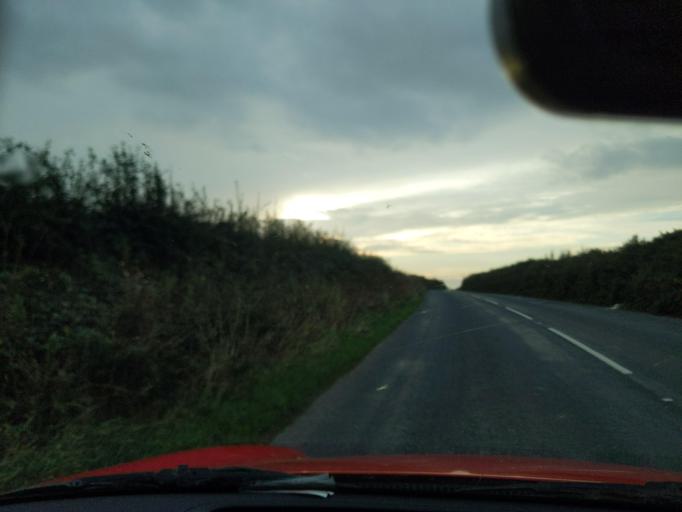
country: GB
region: England
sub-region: Devon
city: Great Torrington
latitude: 50.9121
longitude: -4.1267
